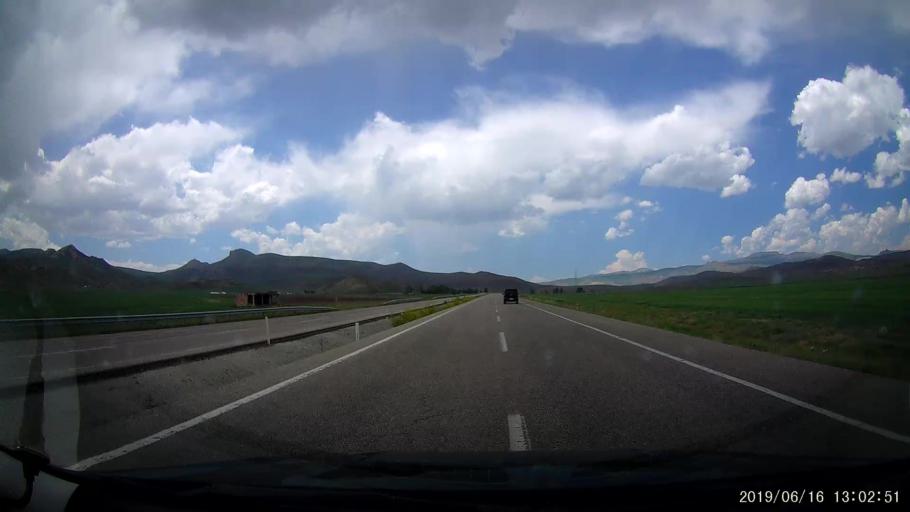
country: TR
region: Agri
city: Sulucem
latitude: 39.5771
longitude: 43.8048
